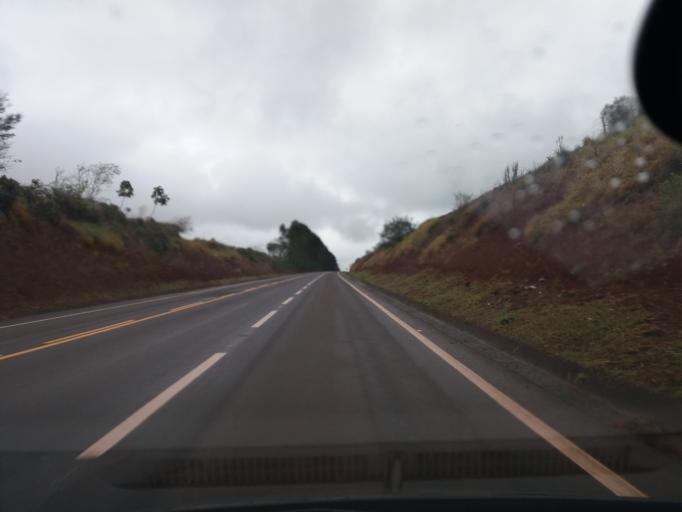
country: BR
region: Parana
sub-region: Campo Mourao
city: Campo Mourao
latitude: -24.0894
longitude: -52.3920
